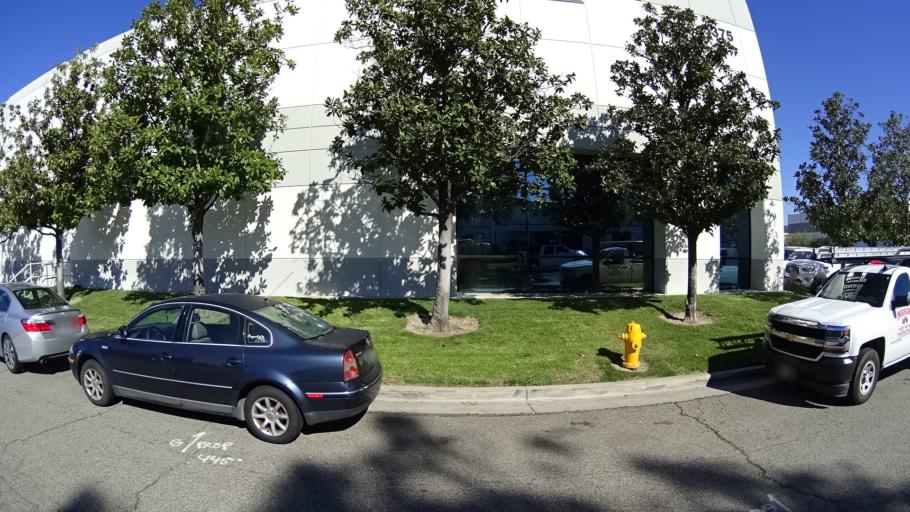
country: US
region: California
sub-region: Orange County
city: Yorba Linda
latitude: 33.8628
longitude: -117.8004
